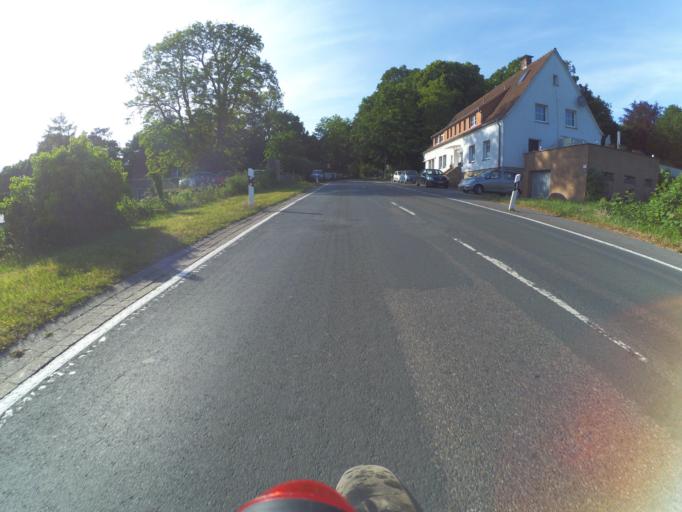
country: DE
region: North Rhine-Westphalia
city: Ibbenburen
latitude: 52.2908
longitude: 7.6992
